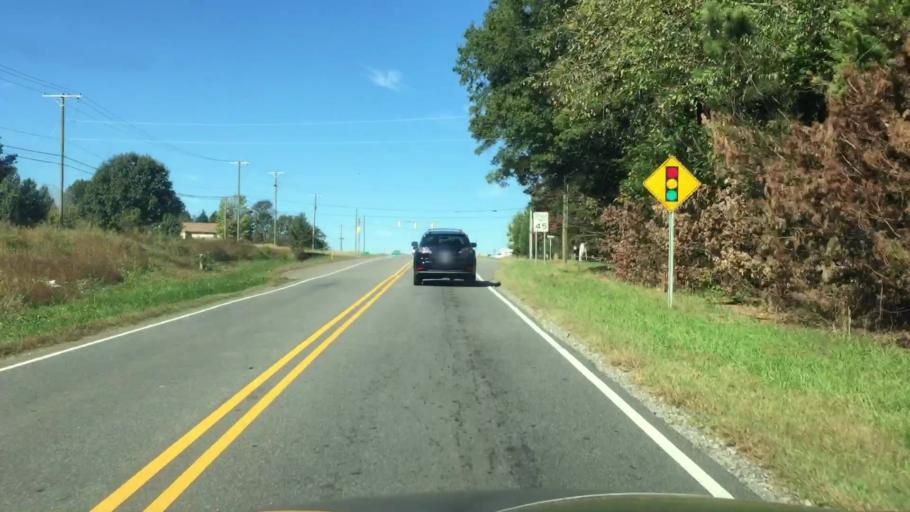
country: US
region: North Carolina
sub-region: Iredell County
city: Mooresville
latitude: 35.5790
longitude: -80.8510
